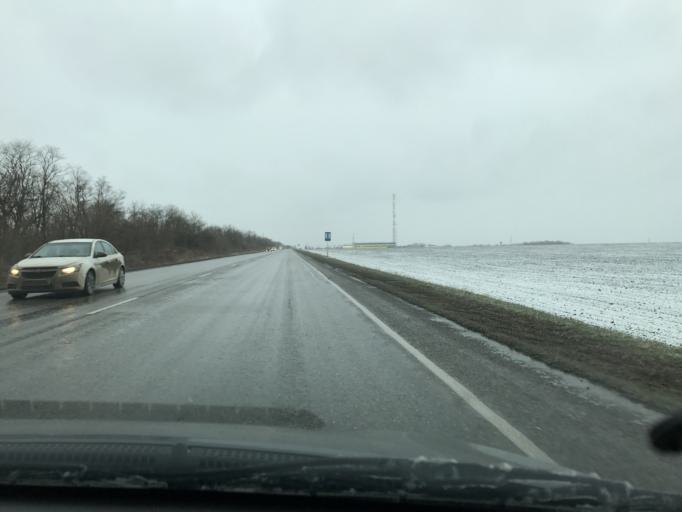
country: RU
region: Rostov
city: Zernograd
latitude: 46.8155
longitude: 40.2732
